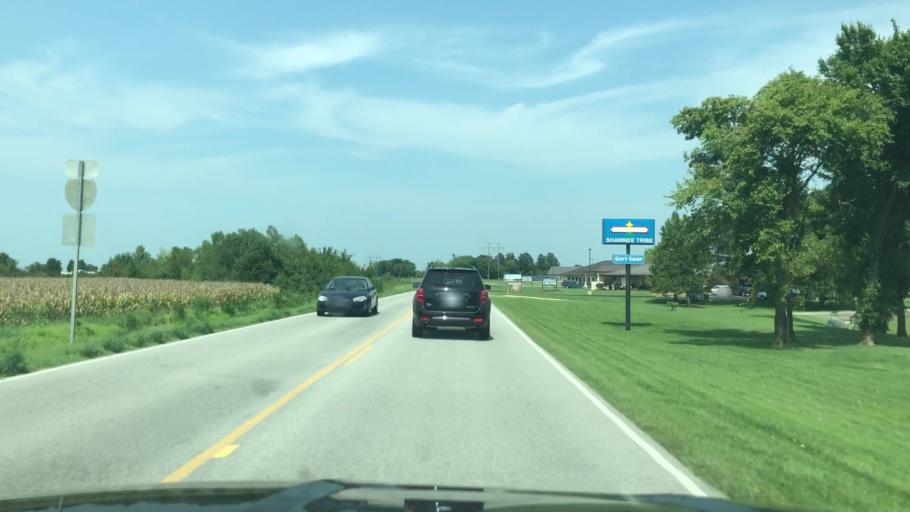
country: US
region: Oklahoma
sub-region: Ottawa County
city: Miami
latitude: 36.8744
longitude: -94.8500
